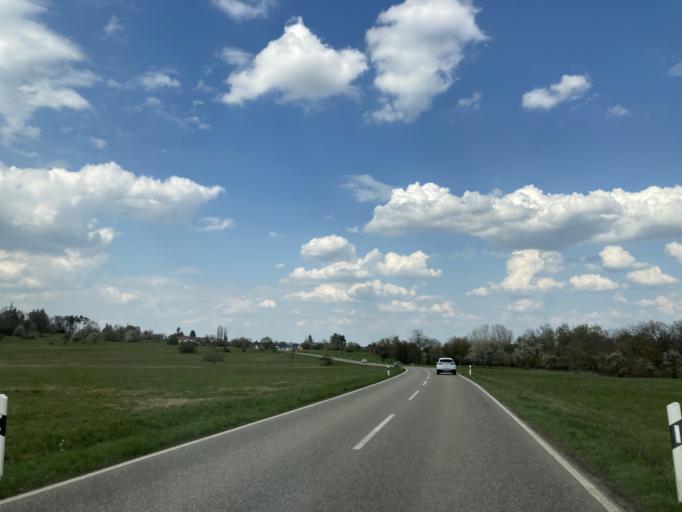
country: DE
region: Baden-Wuerttemberg
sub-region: Karlsruhe Region
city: Dobel
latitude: 48.8570
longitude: 8.4974
